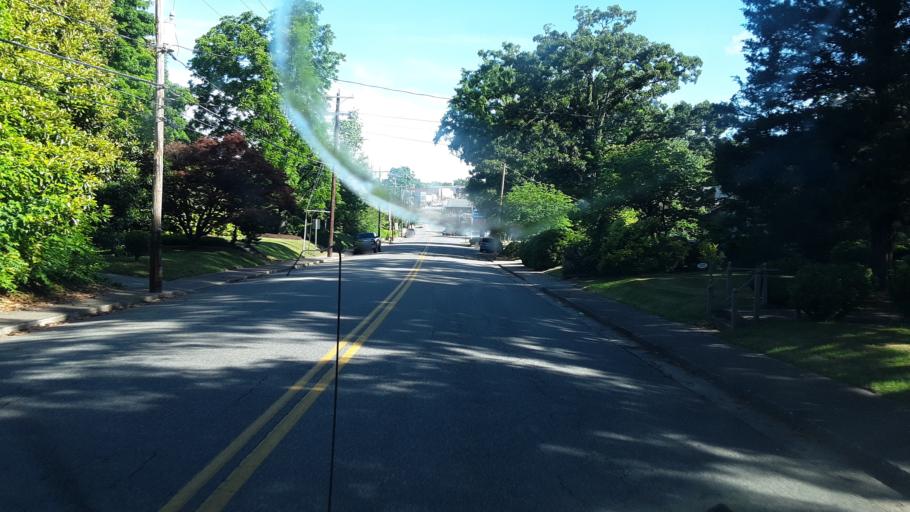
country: US
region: Virginia
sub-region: Pittsylvania County
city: Chatham
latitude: 36.8219
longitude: -79.3962
